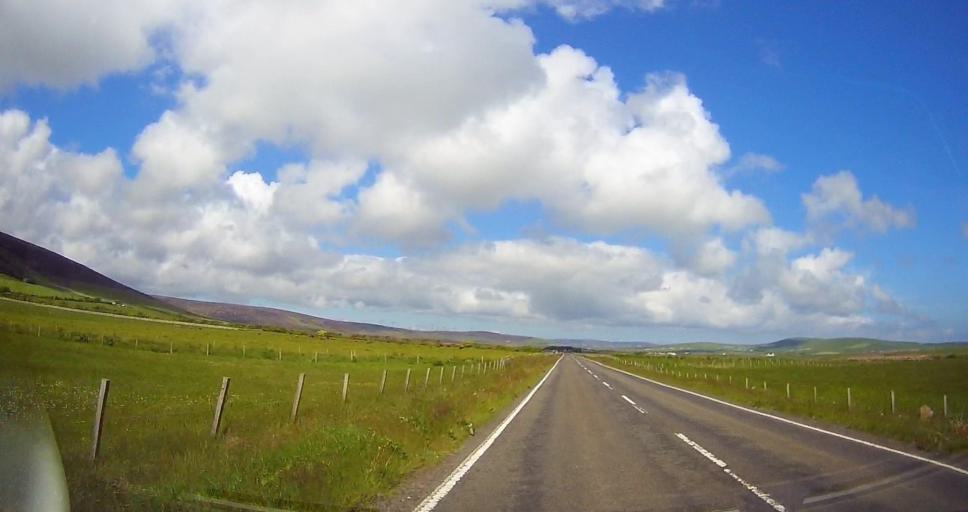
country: GB
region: Scotland
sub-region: Orkney Islands
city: Orkney
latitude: 59.0326
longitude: -3.0916
